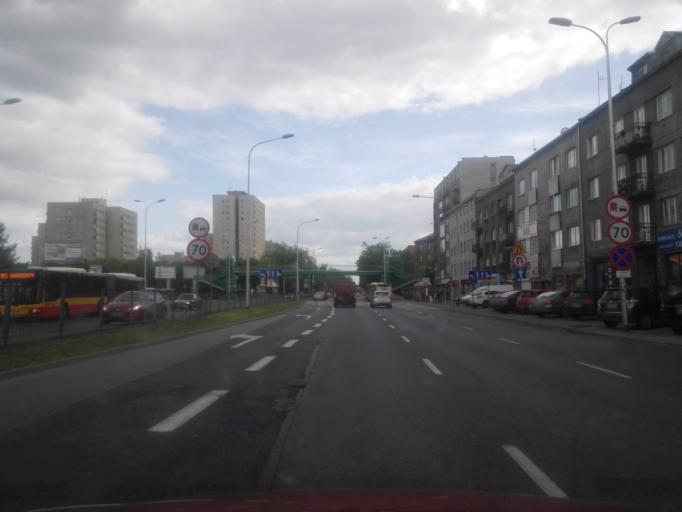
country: PL
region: Masovian Voivodeship
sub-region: Warszawa
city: Mokotow
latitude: 52.2128
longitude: 21.0468
